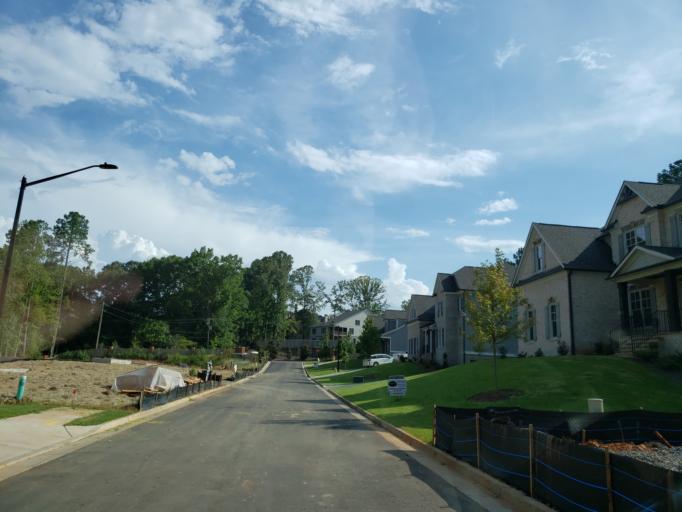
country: US
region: Georgia
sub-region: Cherokee County
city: Woodstock
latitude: 34.0469
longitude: -84.5095
